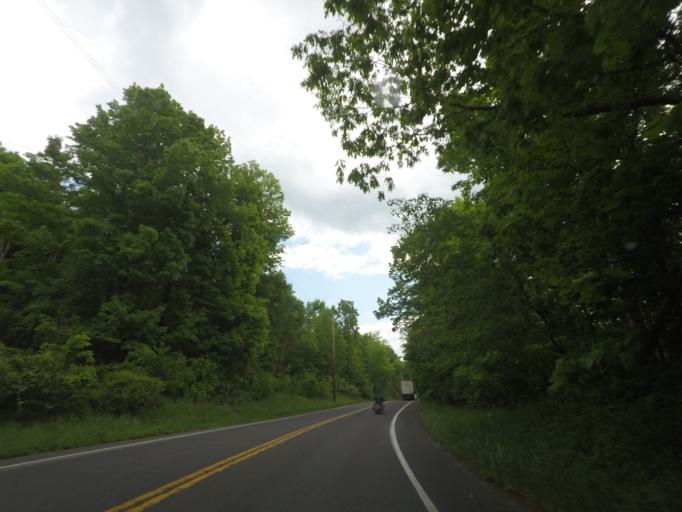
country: US
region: New York
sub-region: Dutchess County
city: Pine Plains
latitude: 42.0717
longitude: -73.6691
